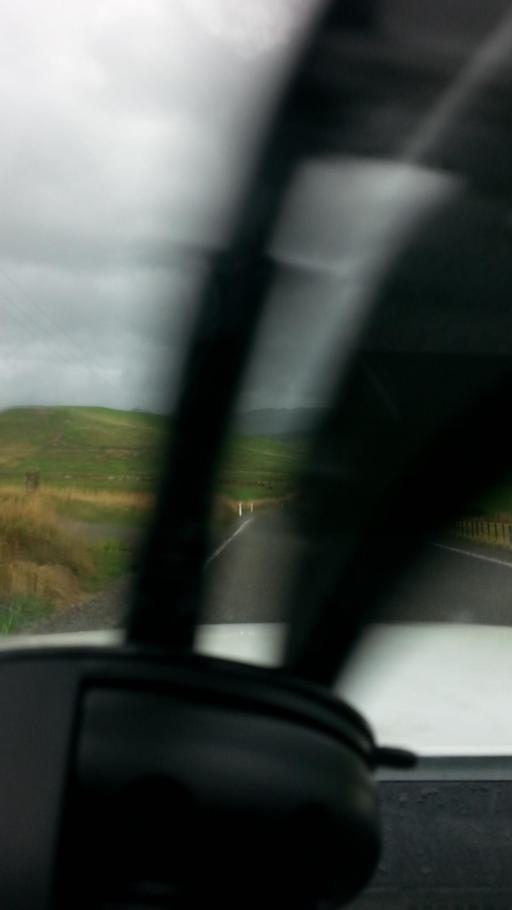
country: NZ
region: Wellington
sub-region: Upper Hutt City
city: Upper Hutt
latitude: -41.4006
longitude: 175.1784
